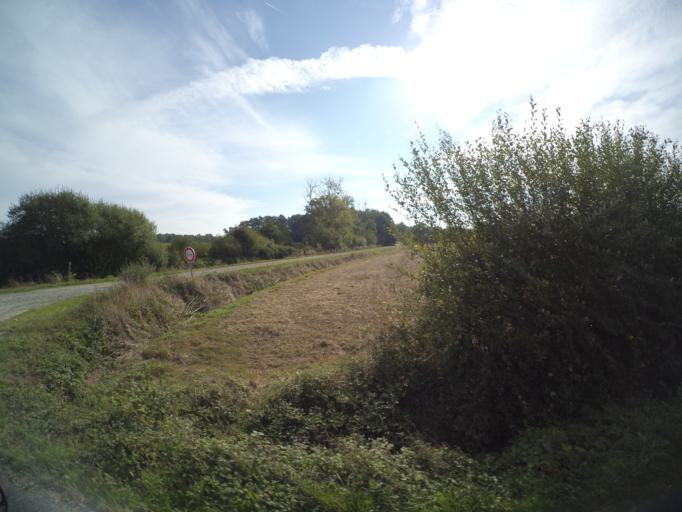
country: FR
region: Pays de la Loire
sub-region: Departement de Maine-et-Loire
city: Tillieres
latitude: 47.1584
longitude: -1.1434
